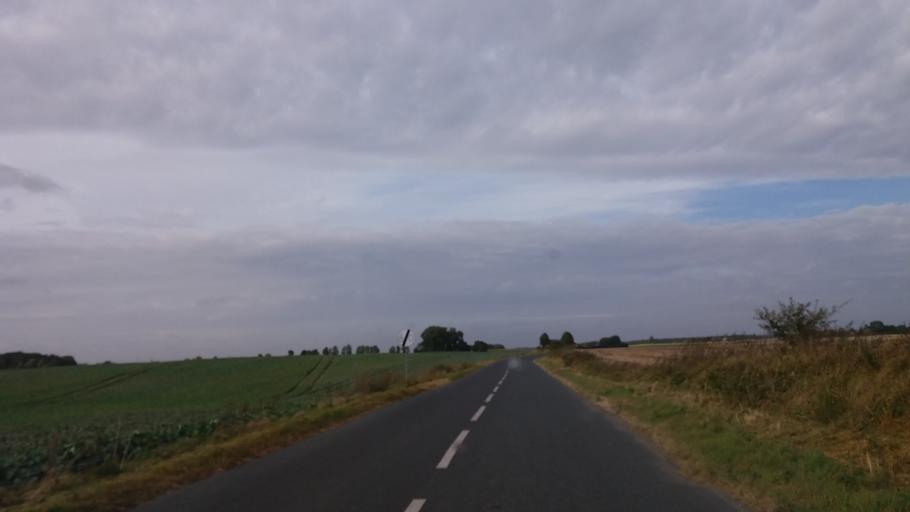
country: PL
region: West Pomeranian Voivodeship
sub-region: Powiat choszczenski
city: Krzecin
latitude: 53.0465
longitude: 15.4921
